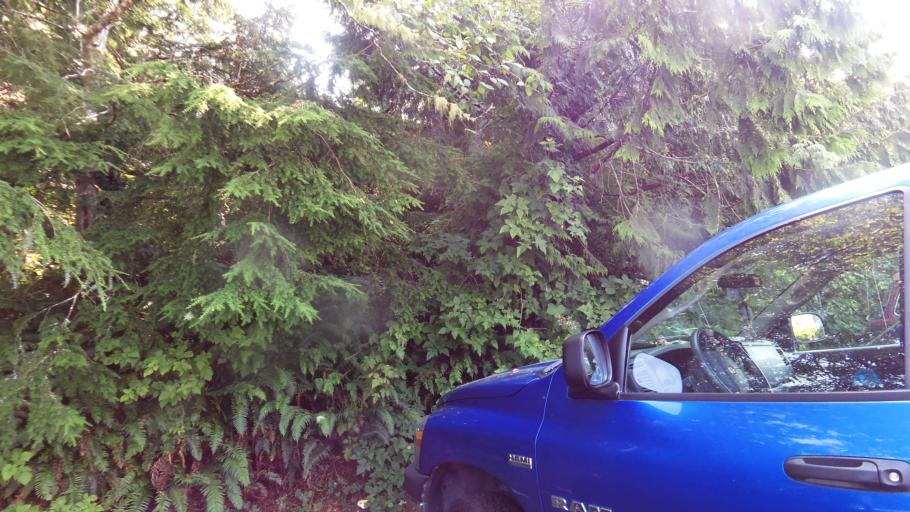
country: CA
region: British Columbia
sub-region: Regional District of Alberni-Clayoquot
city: Tofino
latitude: 49.1524
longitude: -125.9094
